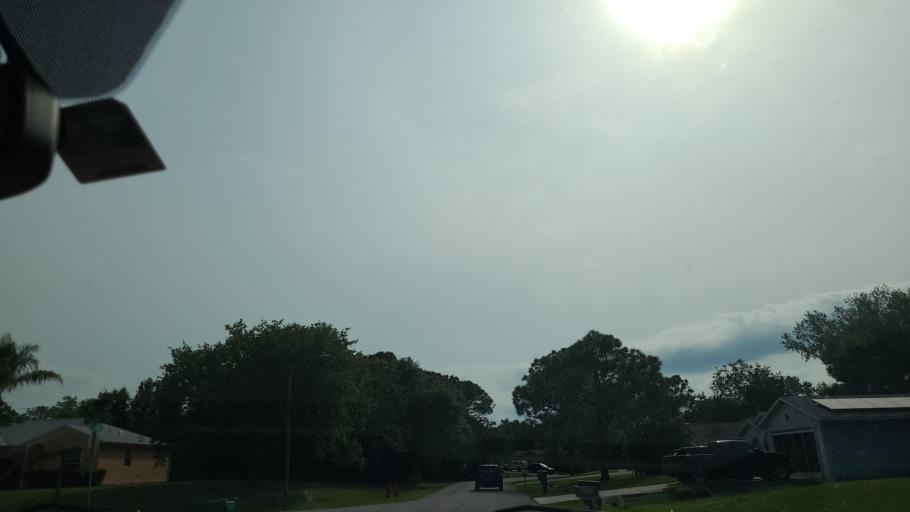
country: US
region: Florida
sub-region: Indian River County
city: Sebastian
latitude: 27.7688
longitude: -80.4913
